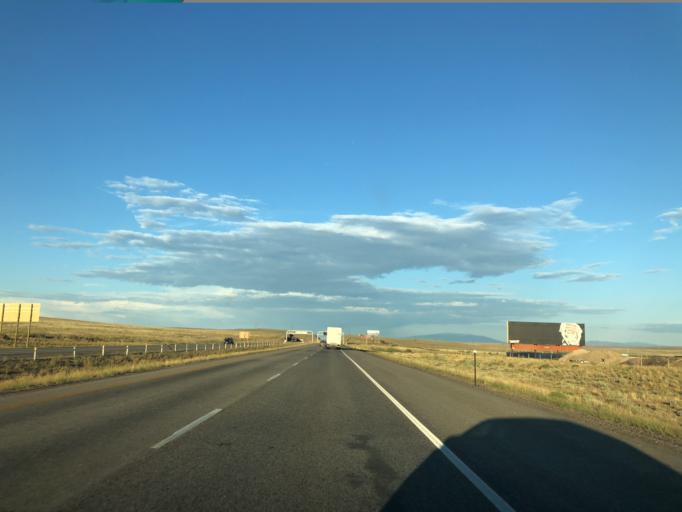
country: US
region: Wyoming
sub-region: Carbon County
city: Rawlins
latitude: 41.7842
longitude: -107.1703
